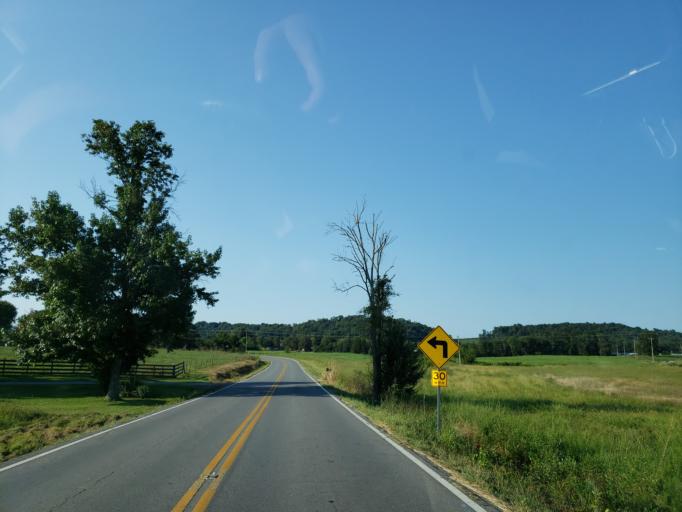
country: US
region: Tennessee
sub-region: Bradley County
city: Wildwood Lake
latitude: 35.0995
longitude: -84.8083
